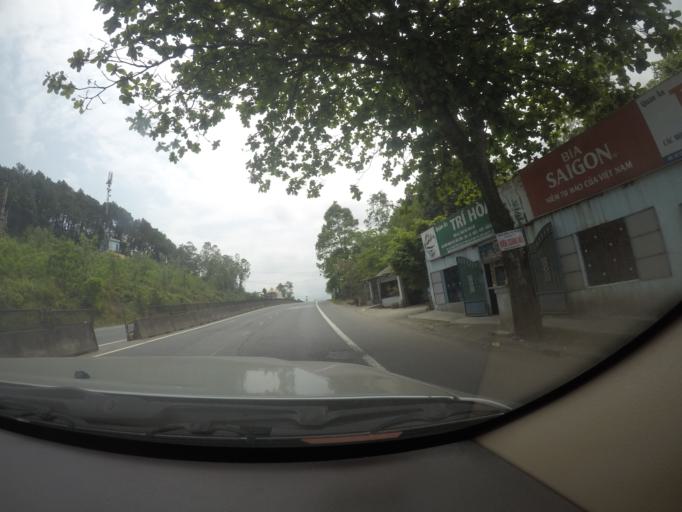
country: VN
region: Thua Thien-Hue
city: Phu Loc
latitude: 16.2887
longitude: 107.8533
